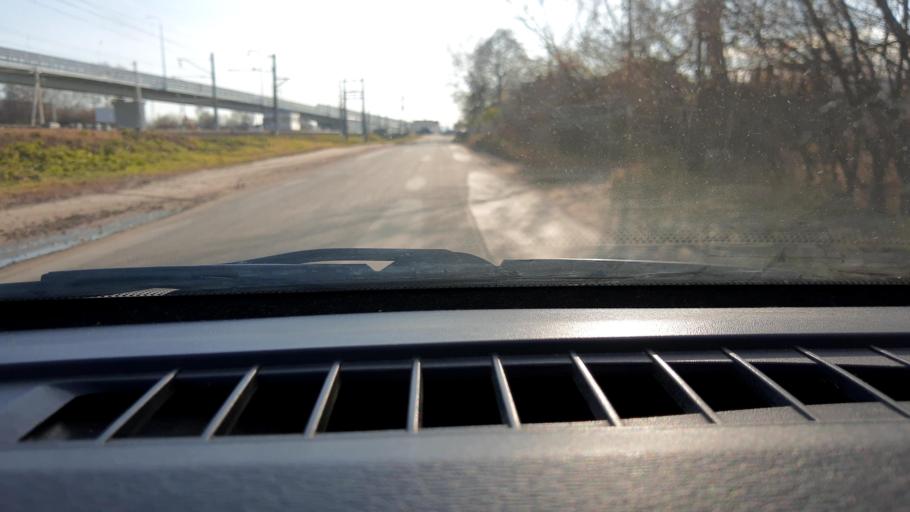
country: RU
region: Nizjnij Novgorod
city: Neklyudovo
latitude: 56.4010
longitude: 43.9813
